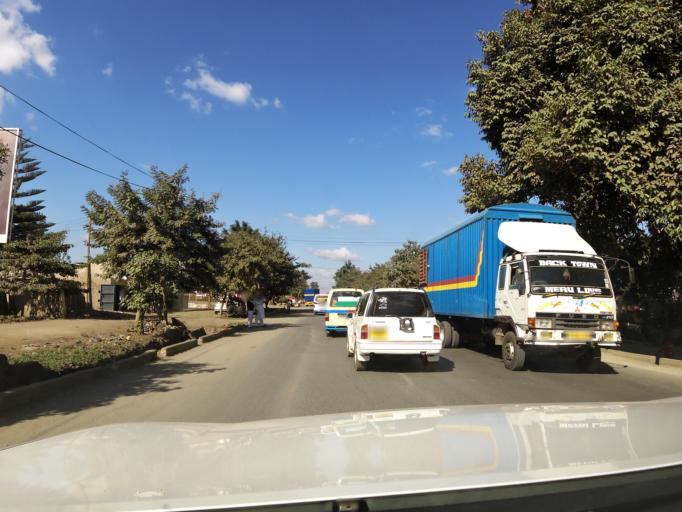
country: TZ
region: Arusha
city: Arusha
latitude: -3.3761
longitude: 36.6632
